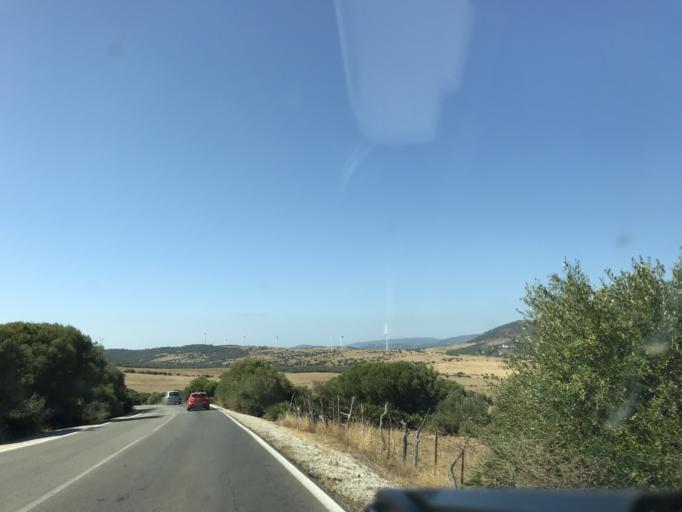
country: ES
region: Andalusia
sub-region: Provincia de Cadiz
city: Zahara de los Atunes
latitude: 36.1025
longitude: -5.7201
